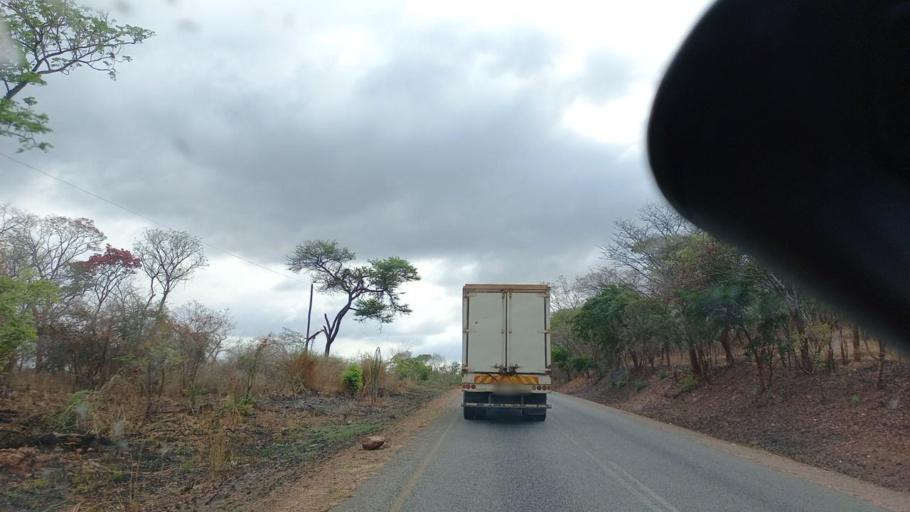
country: ZM
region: Lusaka
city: Chongwe
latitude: -15.1312
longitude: 29.5221
